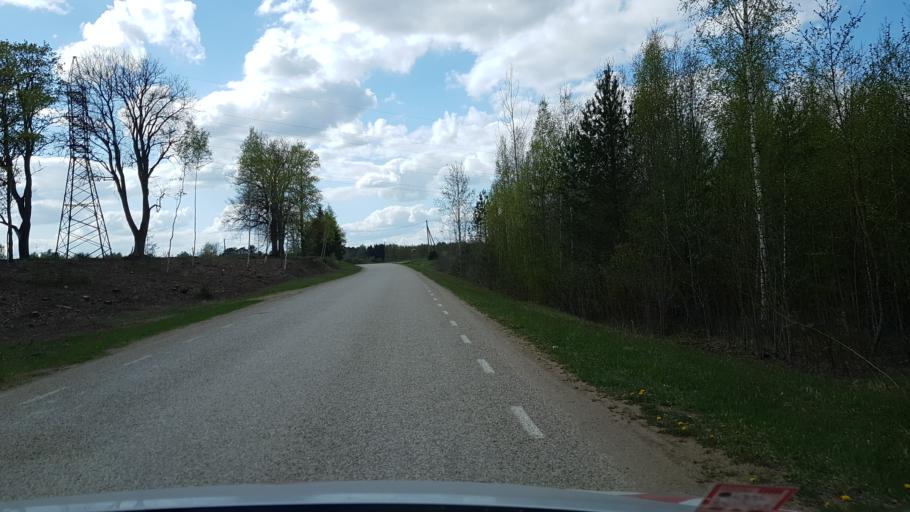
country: EE
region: Tartu
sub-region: UElenurme vald
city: Ulenurme
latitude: 58.3443
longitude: 26.8256
